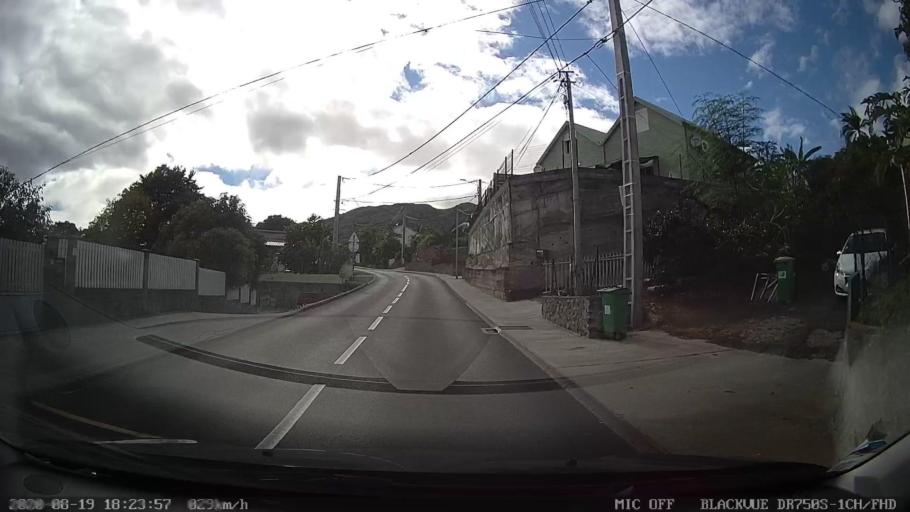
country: RE
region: Reunion
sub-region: Reunion
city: La Possession
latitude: -20.9513
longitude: 55.3437
